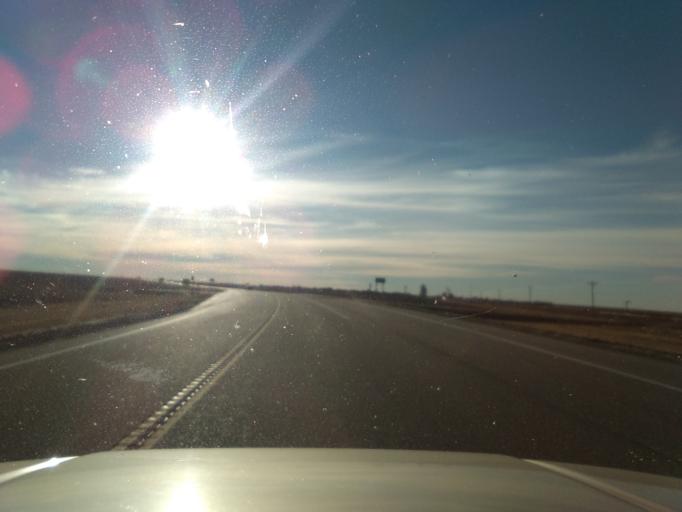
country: US
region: Kansas
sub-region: Sheridan County
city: Hoxie
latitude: 39.4796
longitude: -100.7194
